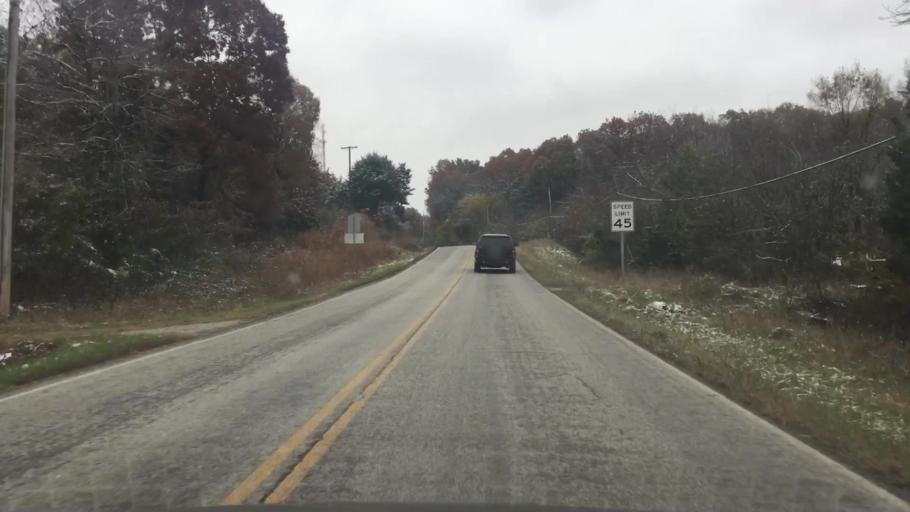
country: US
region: Missouri
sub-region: Saint Clair County
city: Osceola
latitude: 38.0438
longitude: -93.6931
